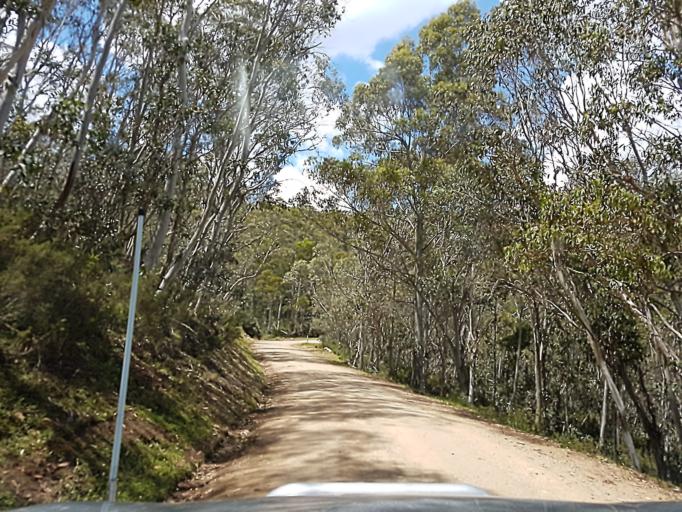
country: AU
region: New South Wales
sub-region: Snowy River
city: Jindabyne
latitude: -36.9136
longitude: 148.1229
